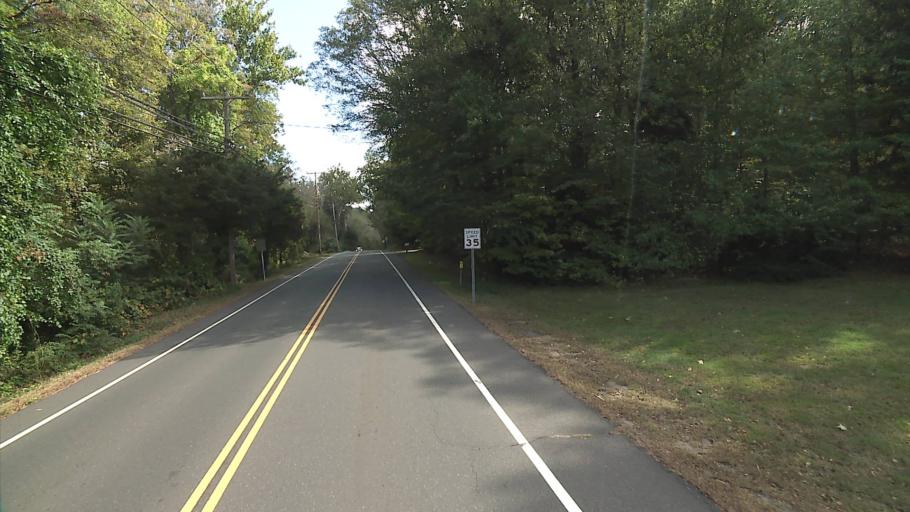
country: US
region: Connecticut
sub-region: Middlesex County
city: Chester Center
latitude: 41.4008
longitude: -72.4899
